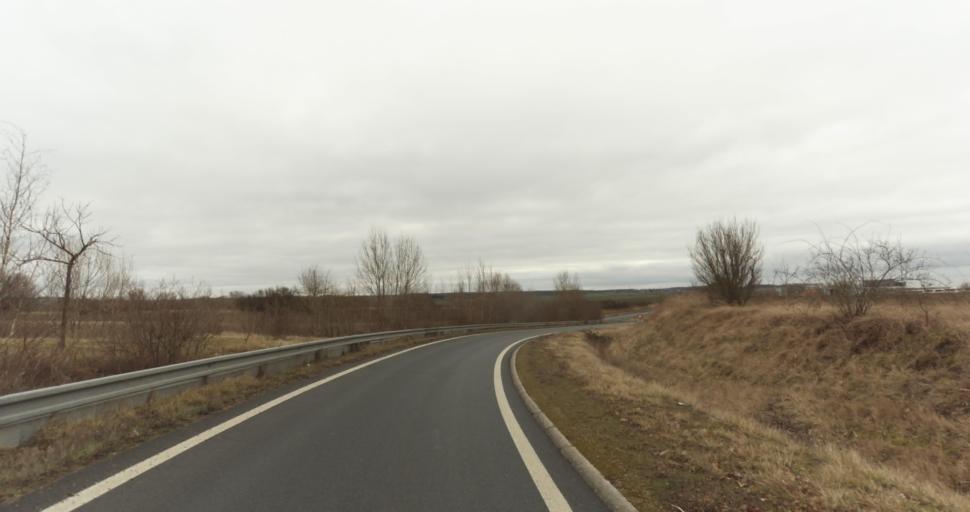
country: FR
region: Pays de la Loire
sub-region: Departement de Maine-et-Loire
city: Doue-la-Fontaine
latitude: 47.1968
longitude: -0.2457
